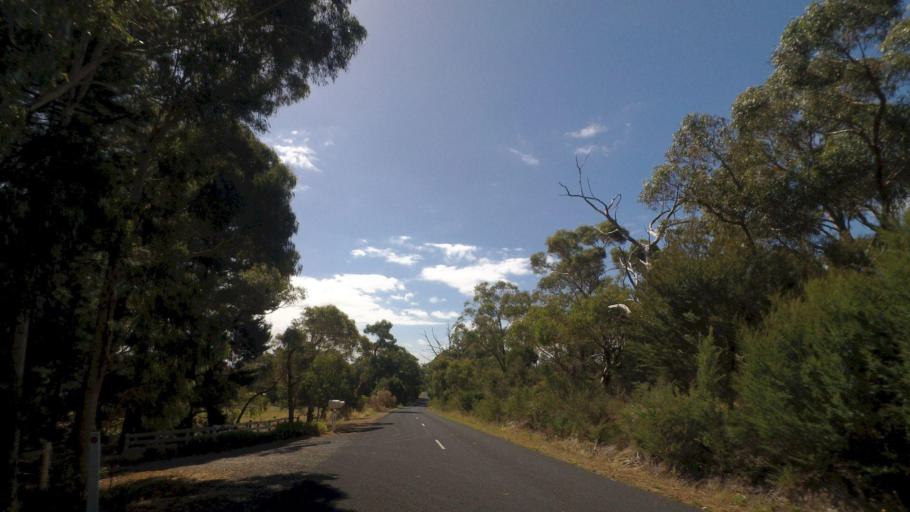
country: AU
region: Victoria
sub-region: Cardinia
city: Koo-Wee-Rup
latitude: -38.2939
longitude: 145.6679
